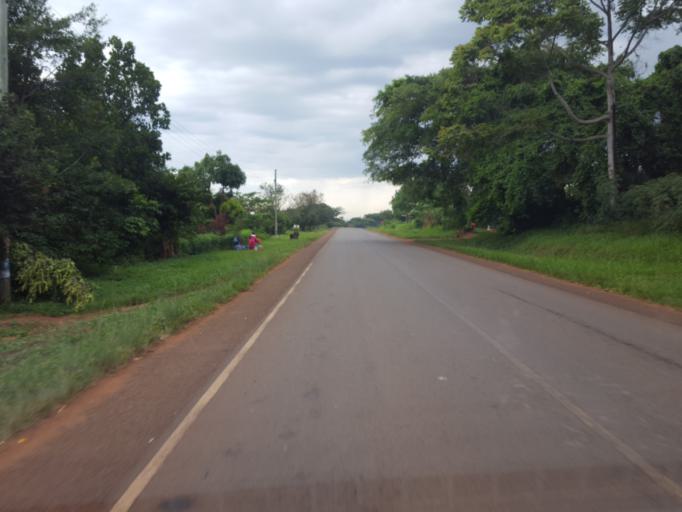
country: UG
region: Central Region
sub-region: Kiboga District
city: Kiboga
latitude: 0.8782
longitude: 31.8439
